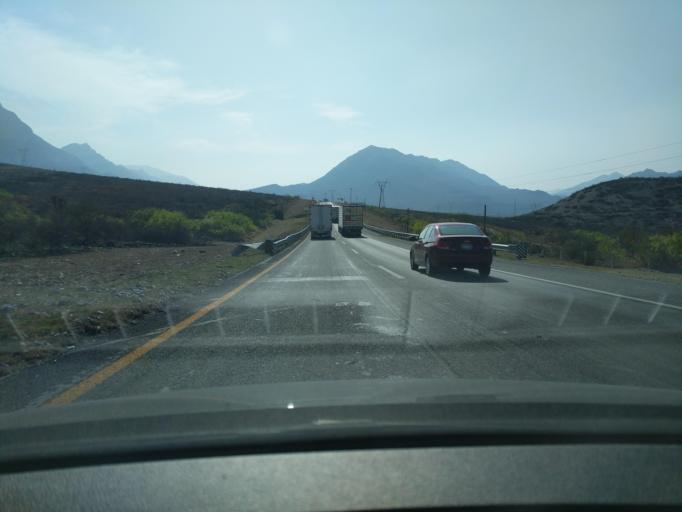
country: MX
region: Nuevo Leon
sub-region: Garcia
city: Las Torres de Guadalupe
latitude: 25.6736
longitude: -100.6877
